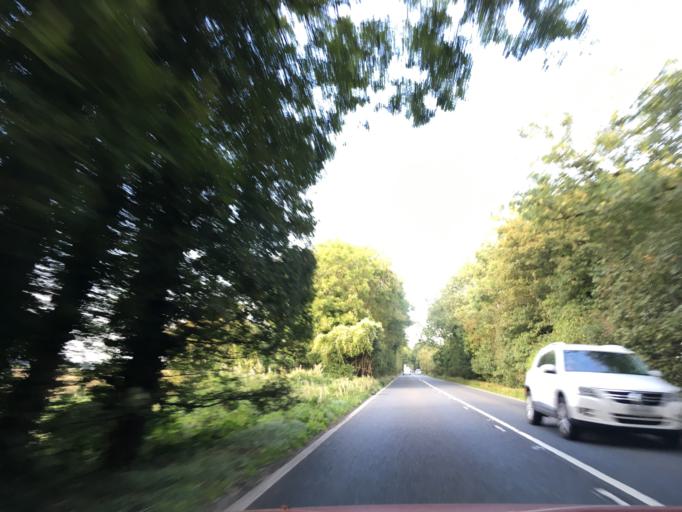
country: GB
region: England
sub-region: Gloucestershire
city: Bourton on the Water
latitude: 51.8715
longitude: -1.7893
